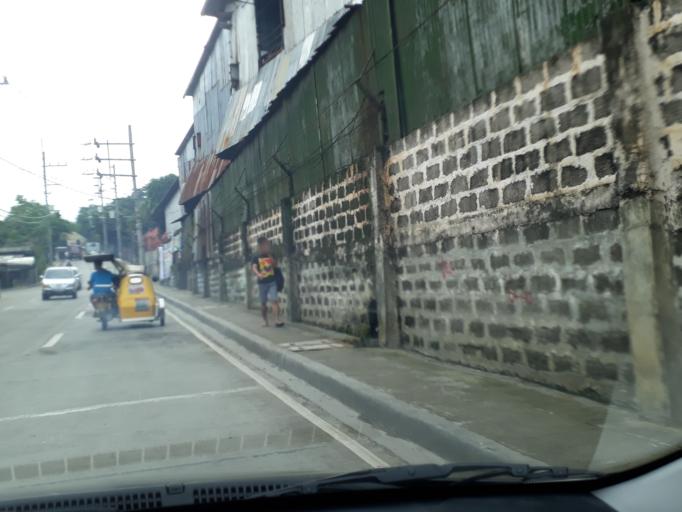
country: PH
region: Calabarzon
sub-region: Province of Rizal
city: Valenzuela
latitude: 14.7163
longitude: 120.9767
